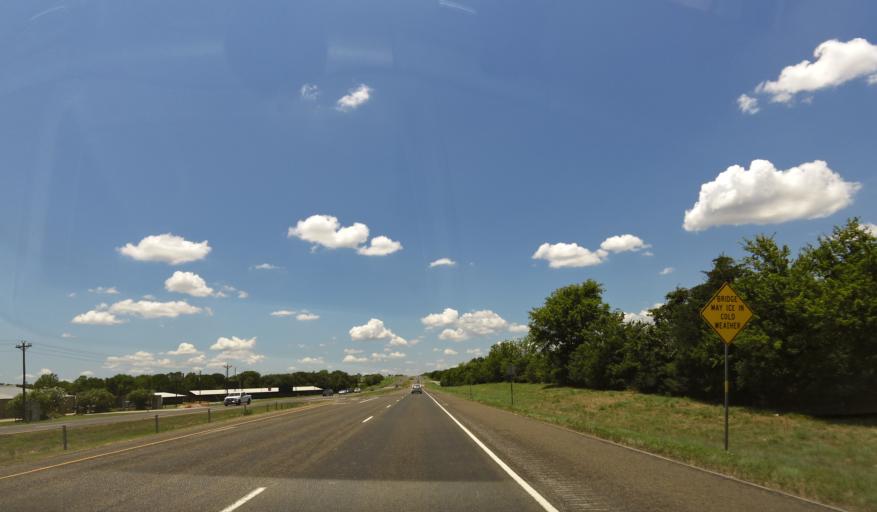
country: US
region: Texas
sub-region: Washington County
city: Brenham
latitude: 30.1902
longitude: -96.5429
